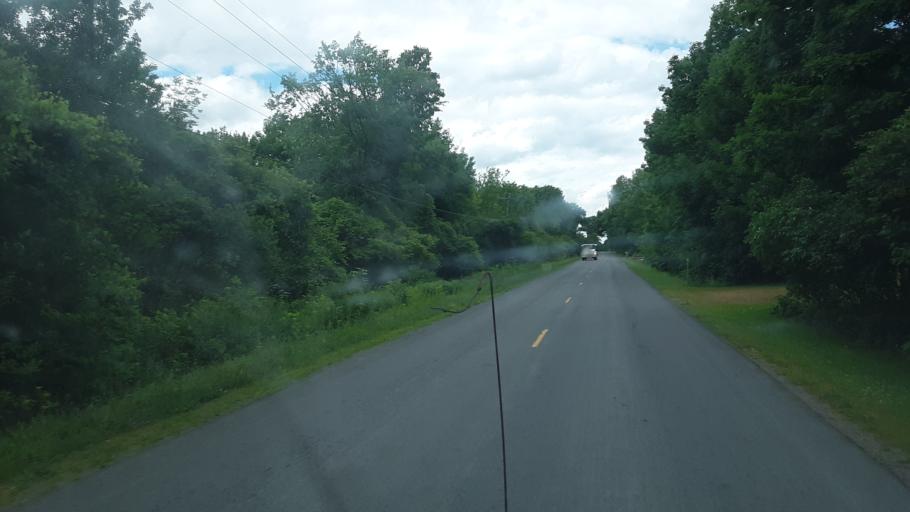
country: US
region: New York
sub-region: Oneida County
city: Rome
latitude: 43.3499
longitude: -75.5536
